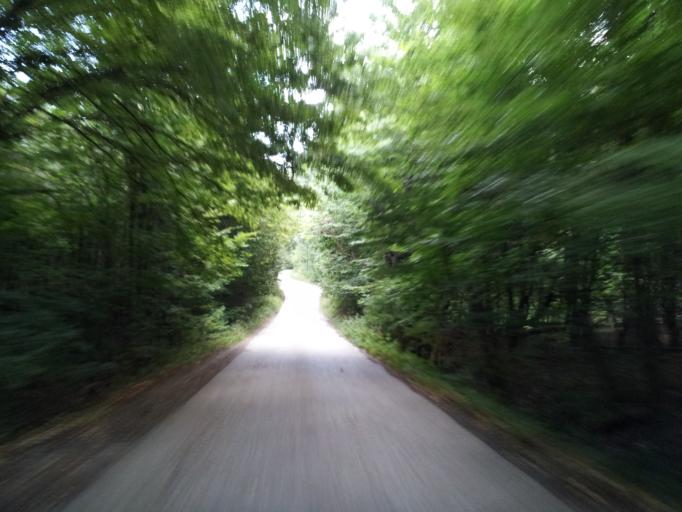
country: HU
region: Pest
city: Kismaros
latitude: 47.8861
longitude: 18.9619
